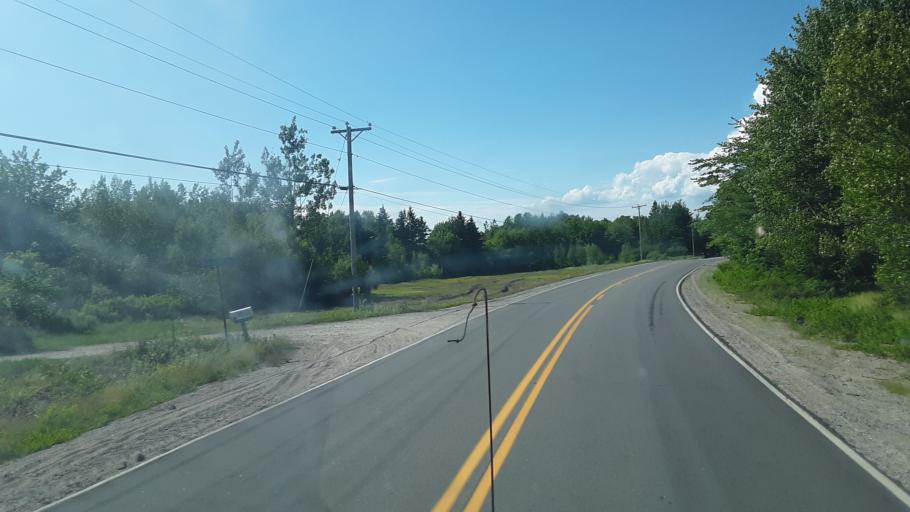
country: US
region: Maine
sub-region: Washington County
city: Cherryfield
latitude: 44.6220
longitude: -67.9359
